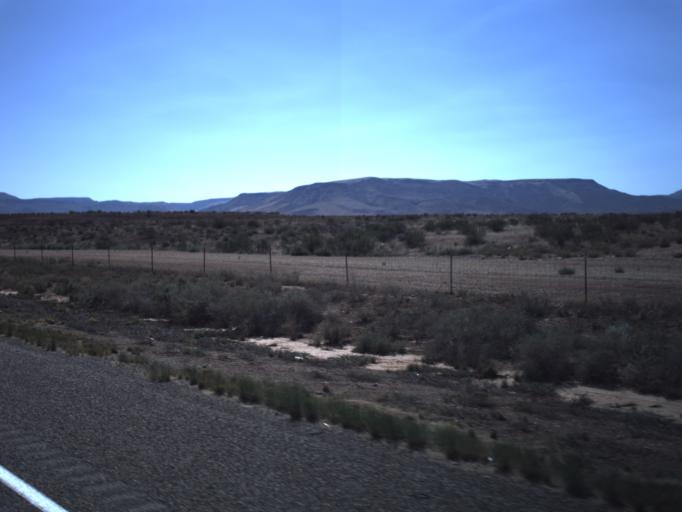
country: US
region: Utah
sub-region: Washington County
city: Saint George
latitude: 37.0105
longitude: -113.5906
